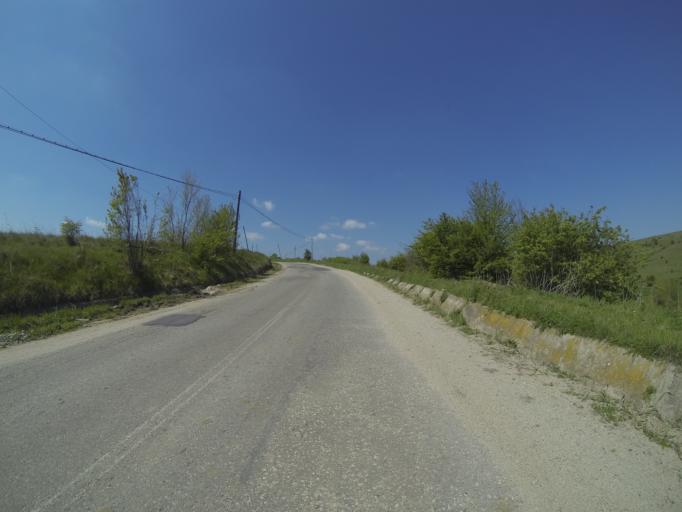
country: RO
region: Dolj
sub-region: Comuna Breasta
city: Breasta
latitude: 44.3034
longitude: 23.6683
